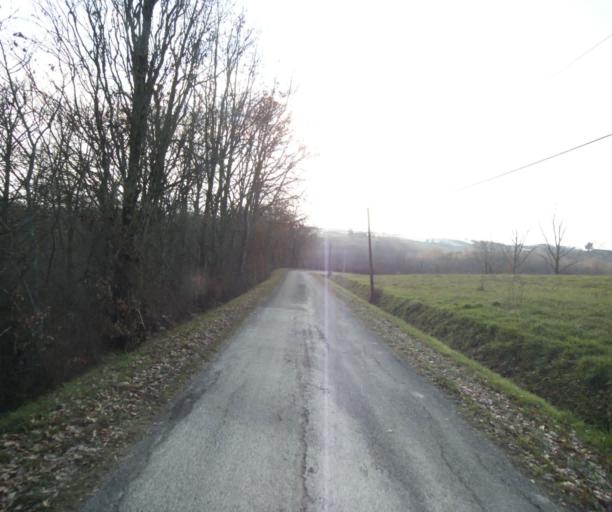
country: FR
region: Midi-Pyrenees
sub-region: Departement du Tarn-et-Garonne
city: Moissac
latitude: 44.1253
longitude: 1.0472
